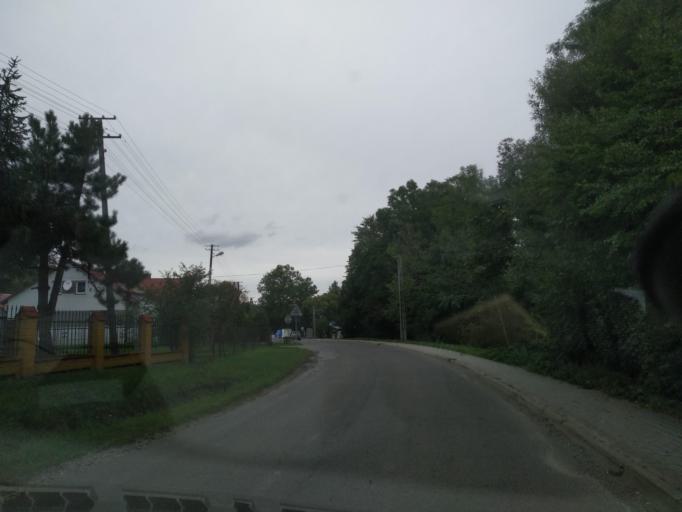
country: PL
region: Subcarpathian Voivodeship
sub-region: Powiat krosnienski
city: Iwonicz-Zdroj
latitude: 49.5811
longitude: 21.7516
